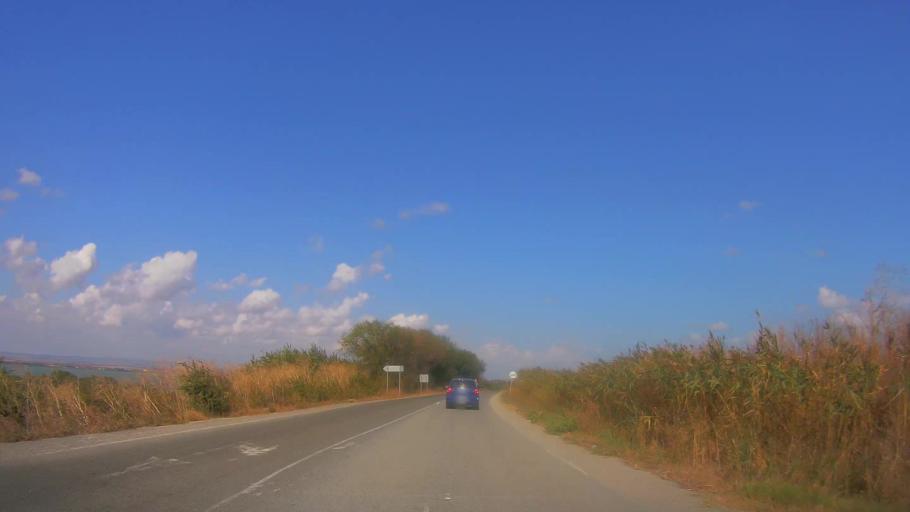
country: BG
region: Burgas
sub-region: Obshtina Burgas
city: Burgas
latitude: 42.4737
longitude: 27.3629
